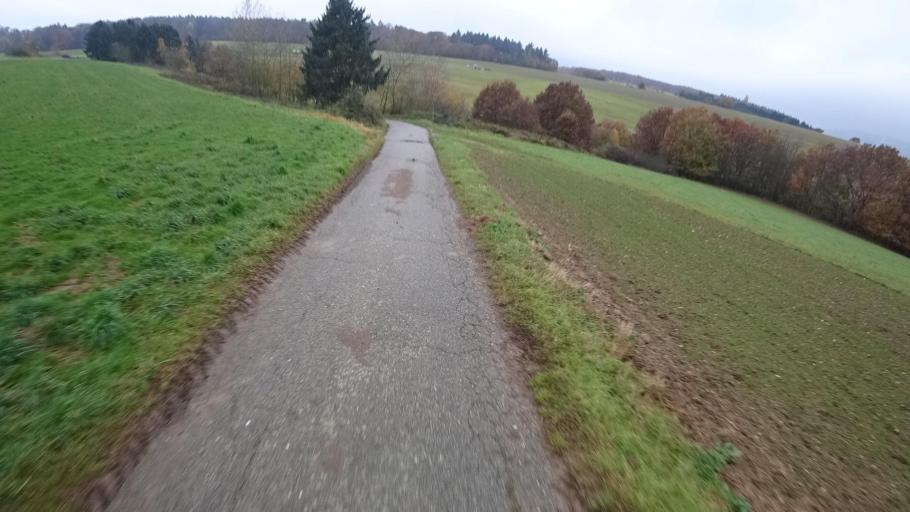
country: DE
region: Rheinland-Pfalz
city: Sankt Goar
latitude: 50.1358
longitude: 7.7021
